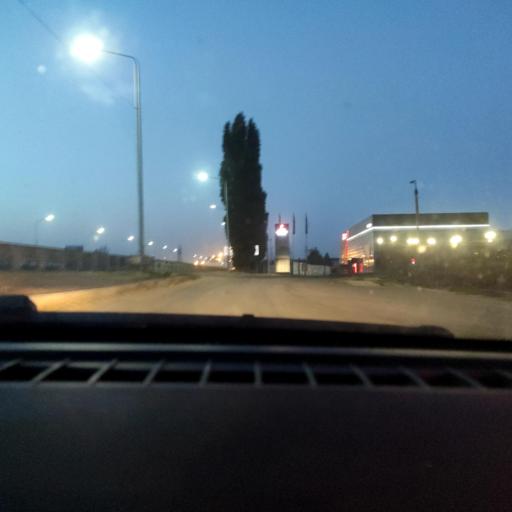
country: RU
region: Voronezj
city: Somovo
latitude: 51.6739
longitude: 39.3004
